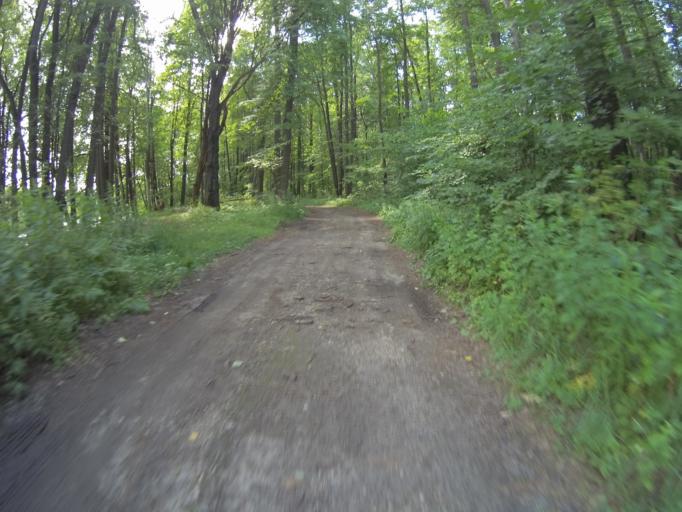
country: RU
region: Vladimir
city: Raduzhnyy
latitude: 56.0524
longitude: 40.3061
